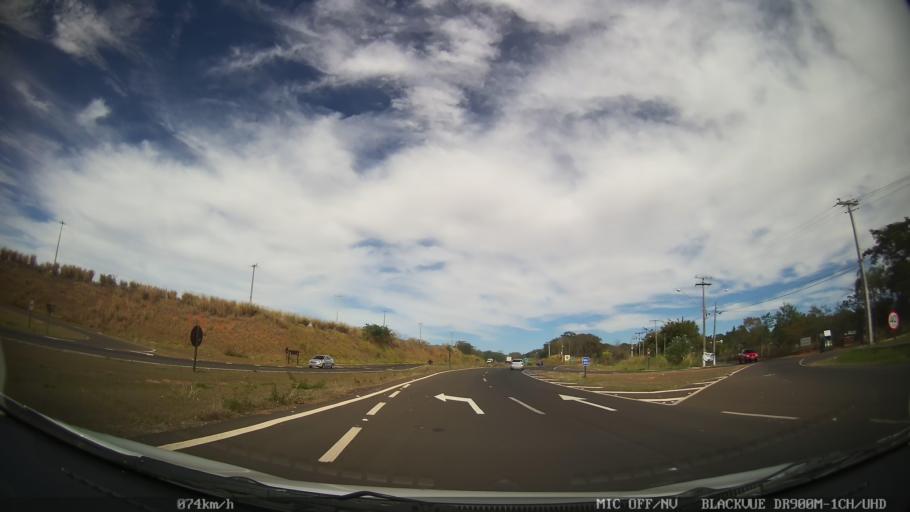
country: BR
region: Sao Paulo
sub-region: Catanduva
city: Catanduva
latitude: -21.1647
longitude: -48.9883
